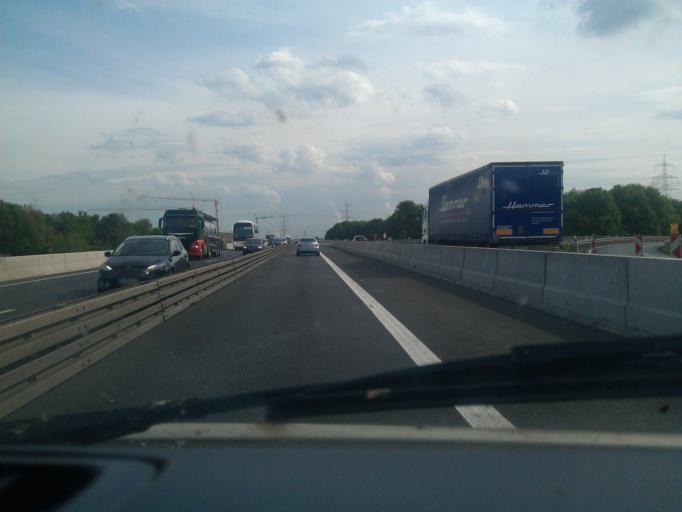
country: DE
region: North Rhine-Westphalia
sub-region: Regierungsbezirk Dusseldorf
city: Kaarst
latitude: 51.2362
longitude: 6.6378
